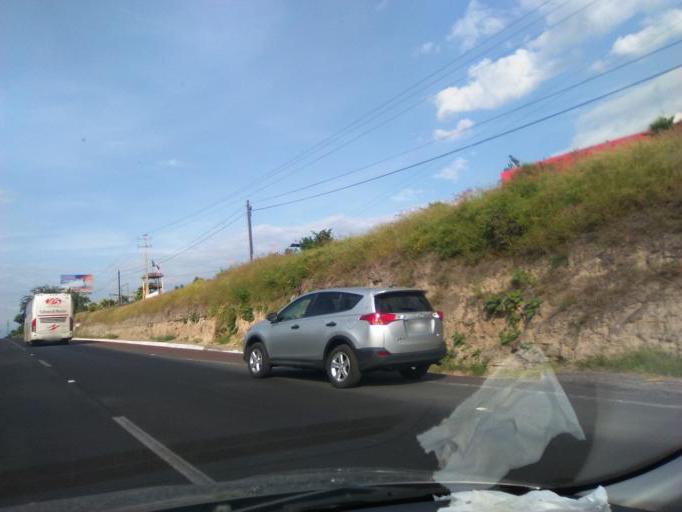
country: MX
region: Morelos
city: Alpuyeca
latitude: 18.7416
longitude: -99.2488
